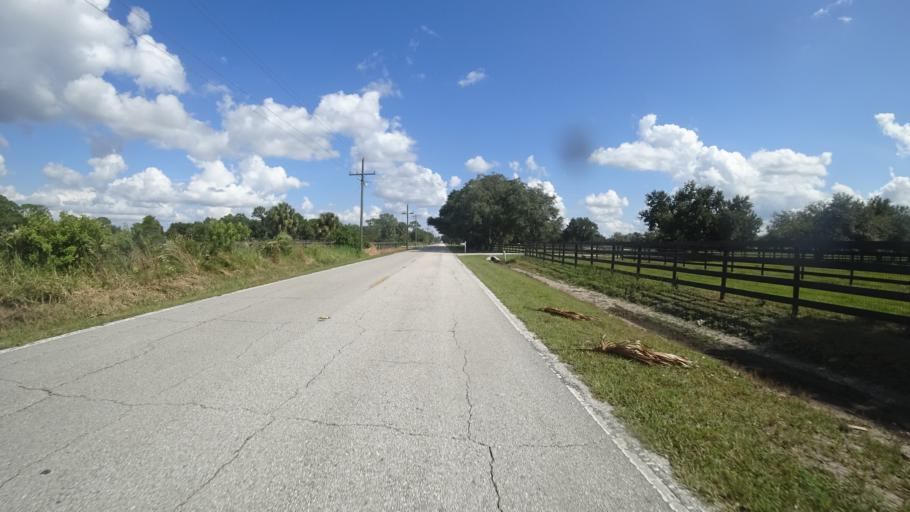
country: US
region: Florida
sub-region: Manatee County
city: Ellenton
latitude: 27.4879
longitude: -82.3871
